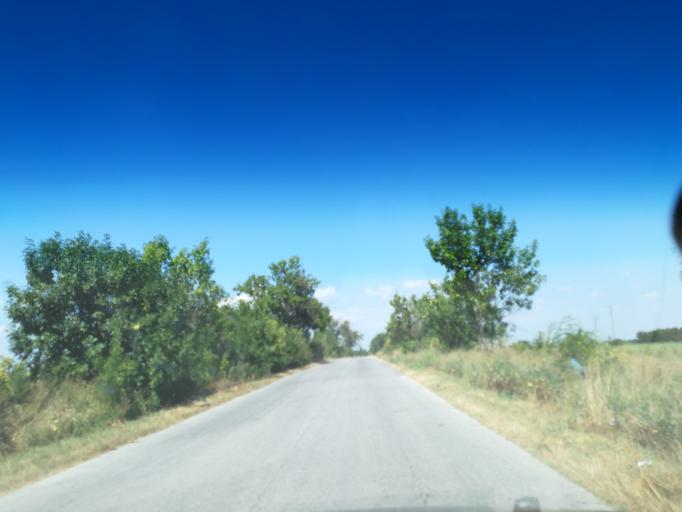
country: BG
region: Stara Zagora
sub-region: Obshtina Chirpan
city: Chirpan
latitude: 42.0564
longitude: 25.1543
